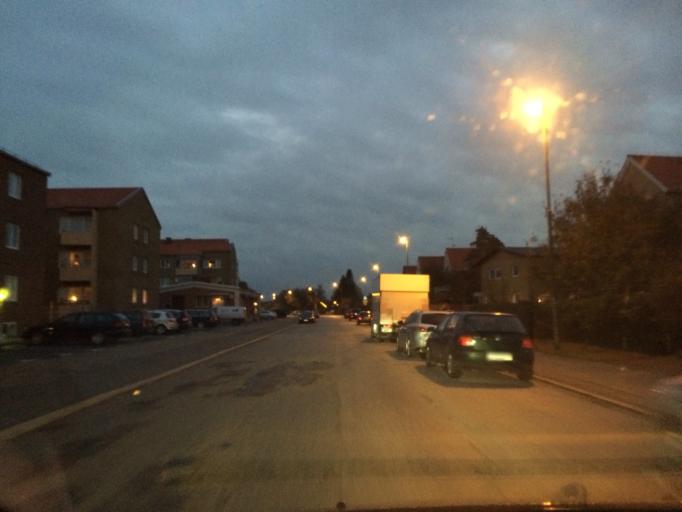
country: SE
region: Skane
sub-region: Malmo
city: Bunkeflostrand
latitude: 55.5819
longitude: 12.9431
